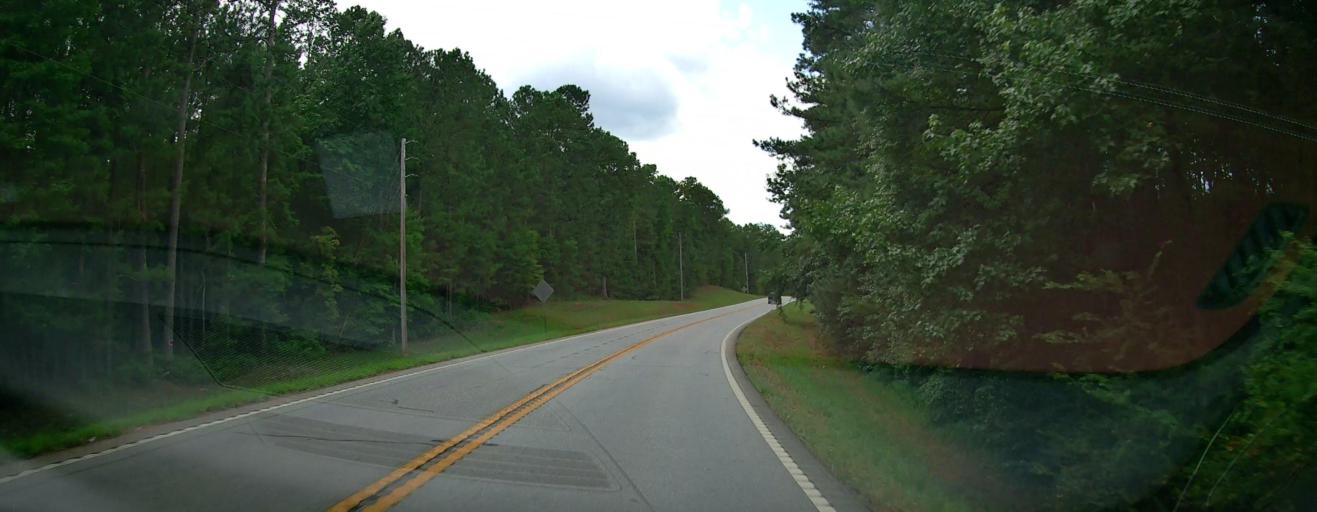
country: US
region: Georgia
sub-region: Heard County
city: Franklin
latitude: 33.3152
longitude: -85.1515
